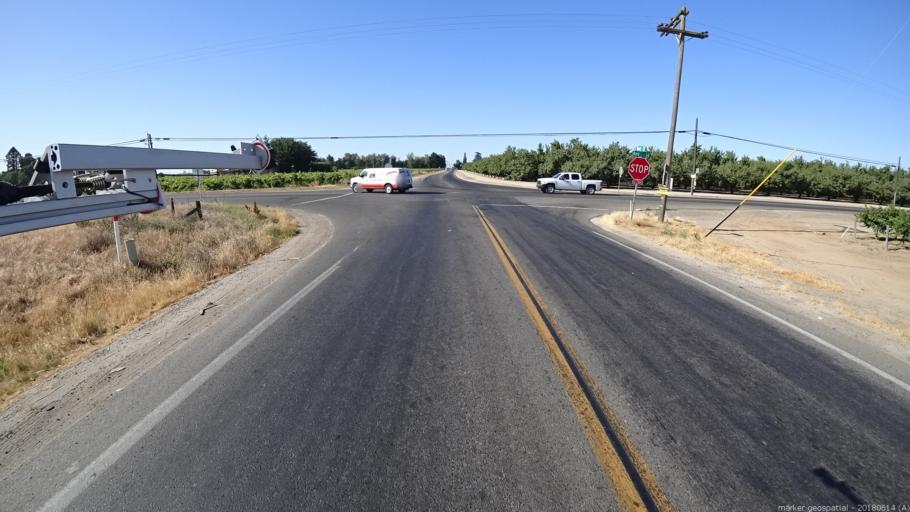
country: US
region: California
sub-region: Madera County
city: Madera
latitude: 36.9531
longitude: -120.1284
